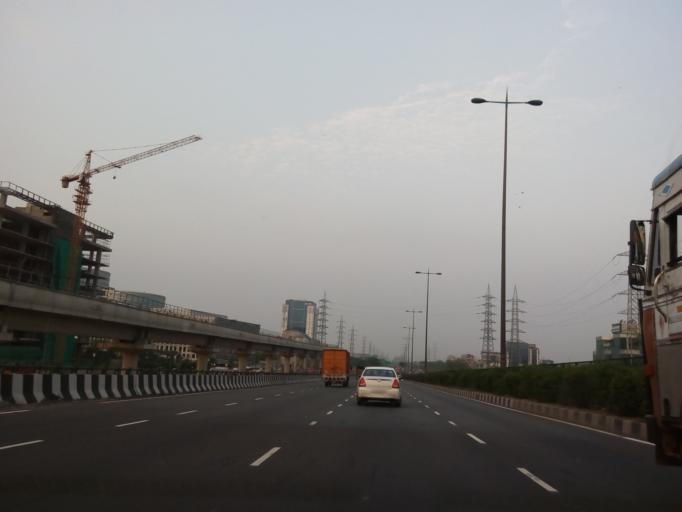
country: IN
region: Haryana
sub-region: Gurgaon
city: Gurgaon
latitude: 28.4978
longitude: 77.0885
